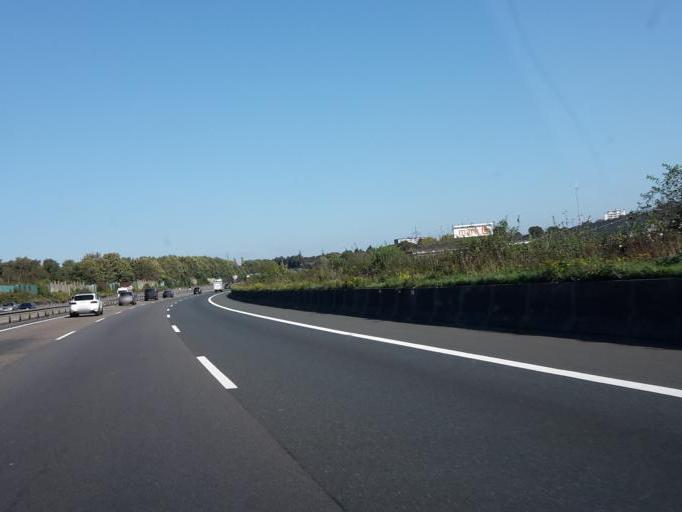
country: DE
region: North Rhine-Westphalia
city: Herdecke
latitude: 51.3968
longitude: 7.4481
